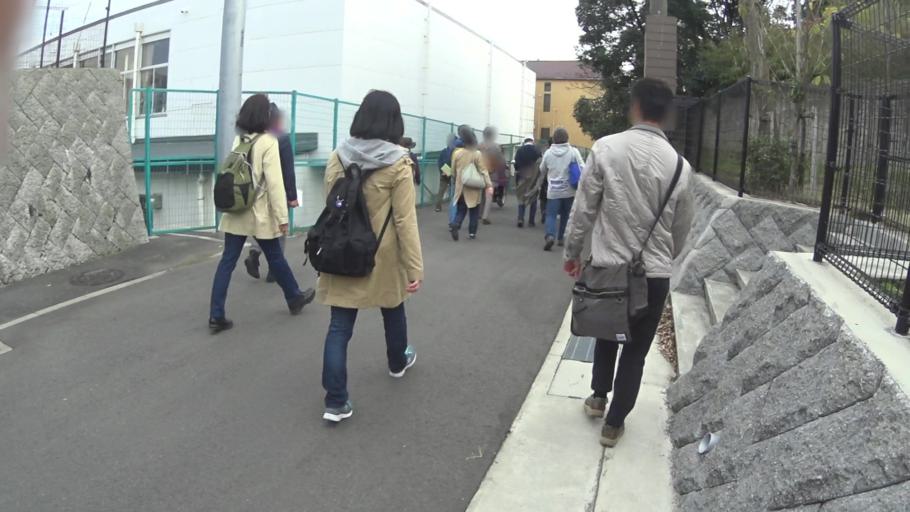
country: JP
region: Kanagawa
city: Fujisawa
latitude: 35.3127
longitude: 139.4919
